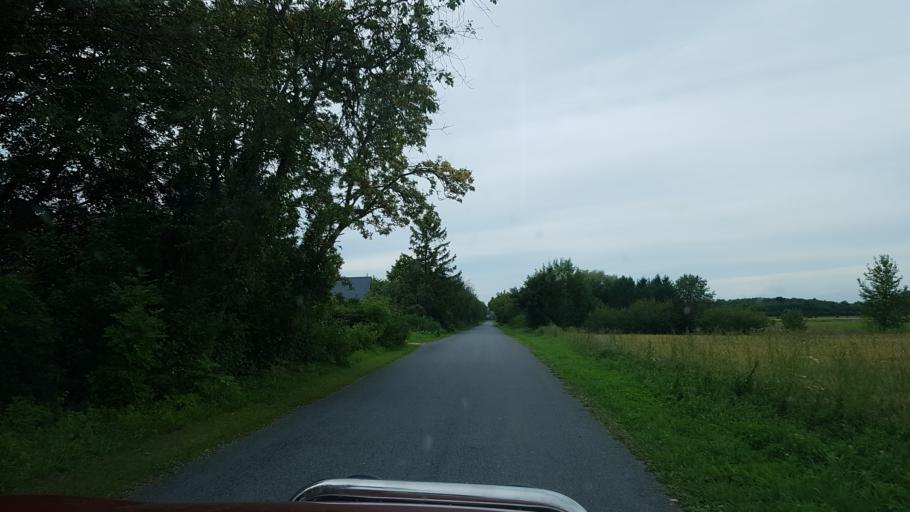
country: EE
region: Laeaene
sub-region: Ridala Parish
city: Uuemoisa
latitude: 58.7928
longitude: 23.6617
